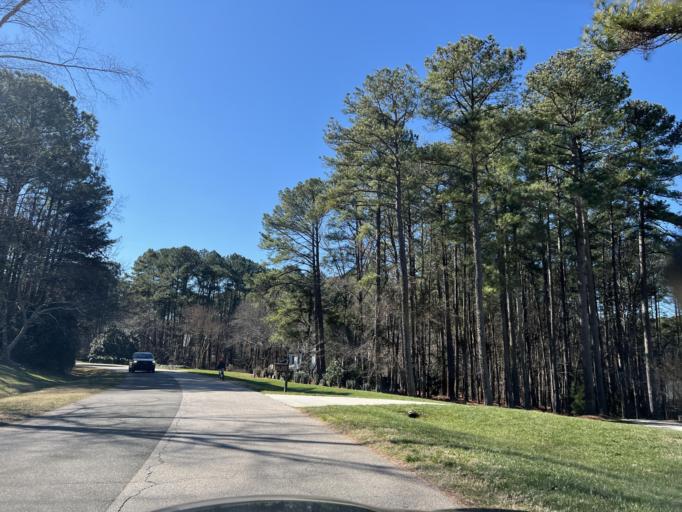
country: US
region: North Carolina
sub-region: Wake County
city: Wake Forest
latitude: 35.9101
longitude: -78.6165
